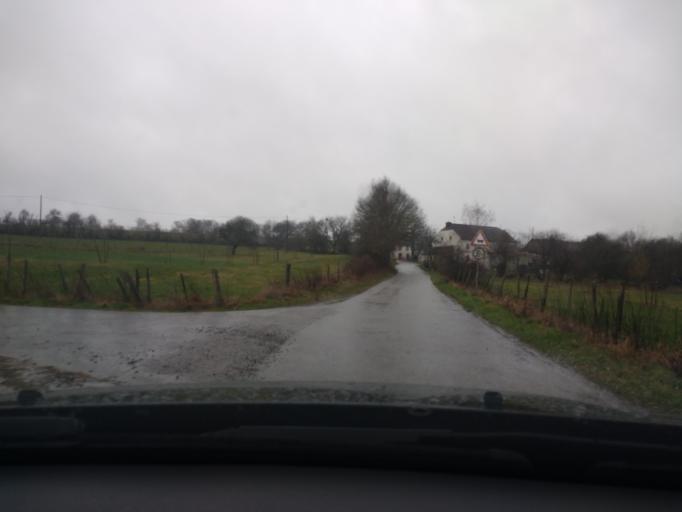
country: DE
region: Rheinland-Pfalz
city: Lampaden
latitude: 49.6663
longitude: 6.6997
